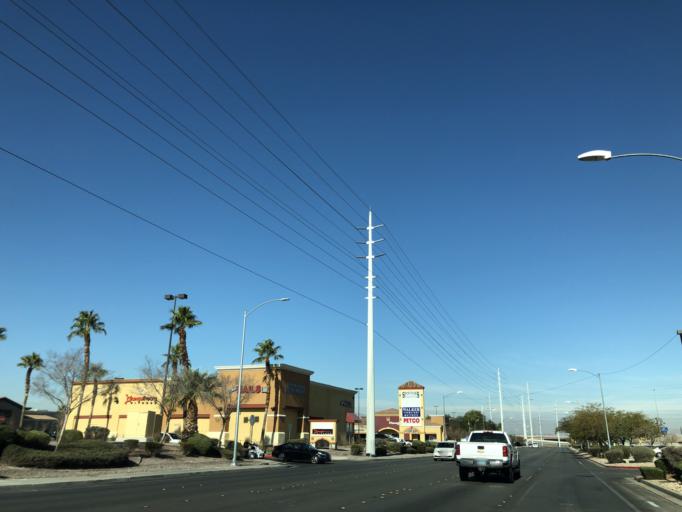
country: US
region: Nevada
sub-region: Clark County
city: Whitney
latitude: 36.0662
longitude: -115.0363
